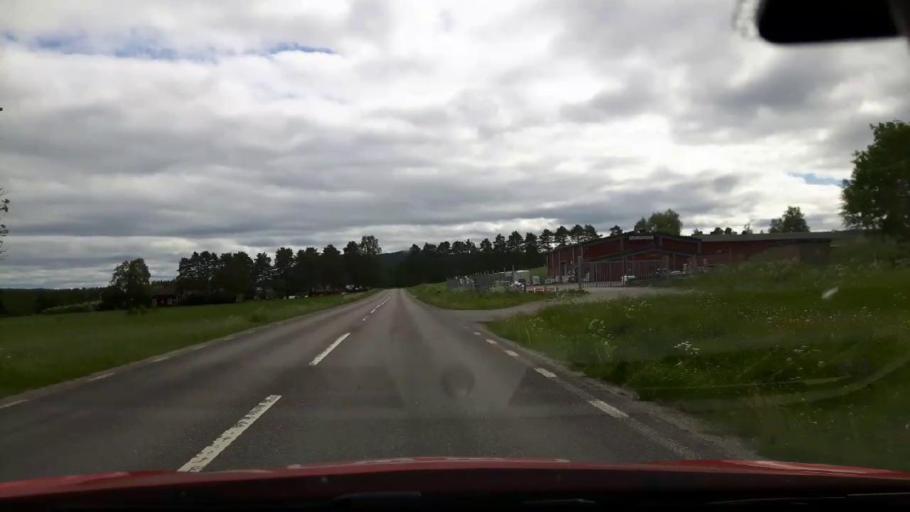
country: SE
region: Jaemtland
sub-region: Ragunda Kommun
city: Hammarstrand
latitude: 63.0985
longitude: 16.3575
